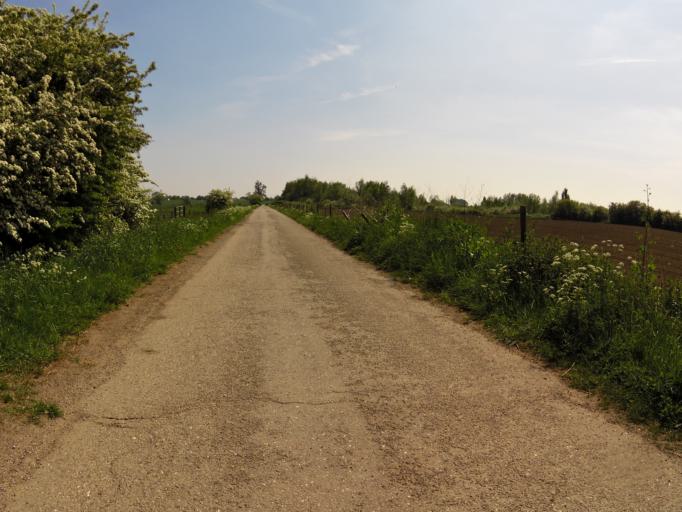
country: NL
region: Gelderland
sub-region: Gemeente Neerijnen
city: Neerijnen
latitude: 51.8149
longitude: 5.3014
